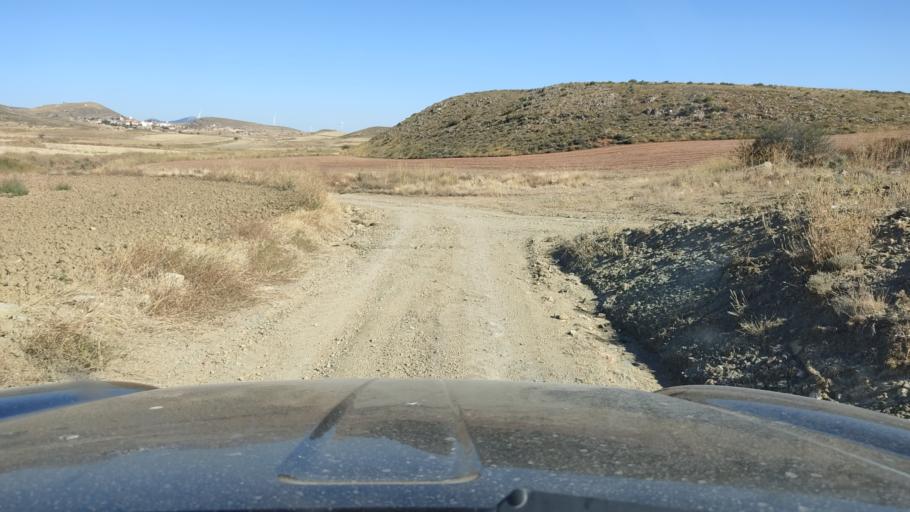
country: ES
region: Aragon
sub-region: Provincia de Teruel
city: Monforte de Moyuela
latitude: 41.0372
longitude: -0.9978
